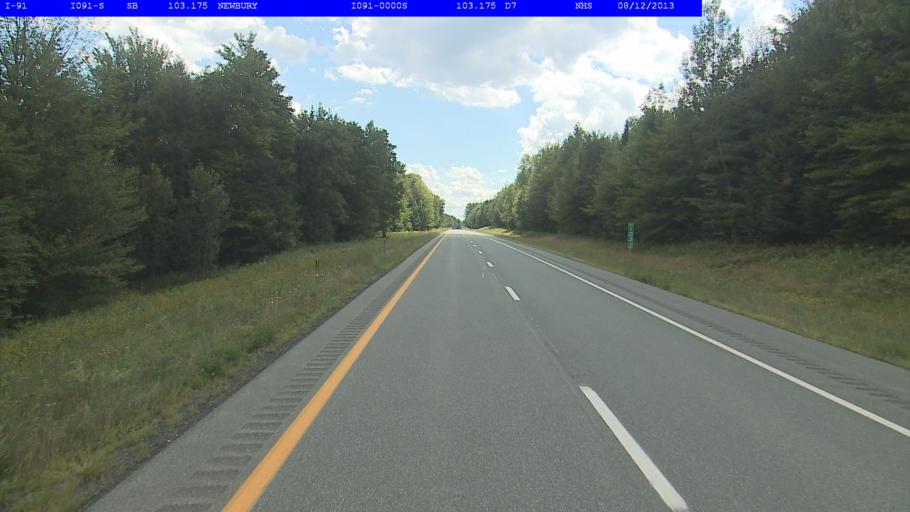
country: US
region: New Hampshire
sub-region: Grafton County
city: Haverhill
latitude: 44.0596
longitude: -72.1088
